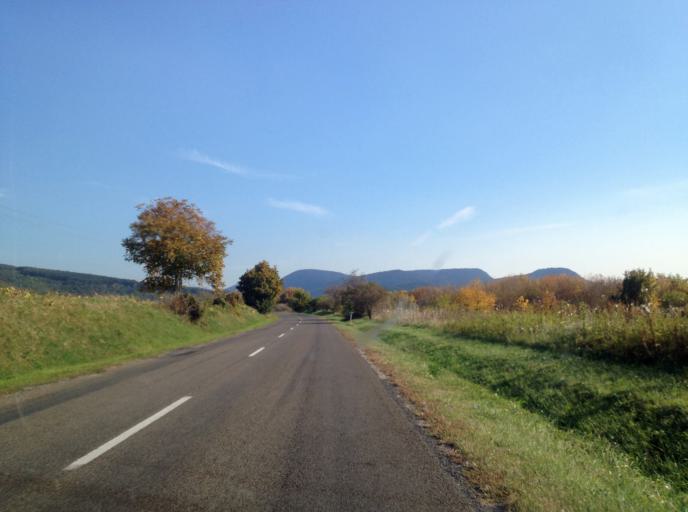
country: HU
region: Komarom-Esztergom
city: Esztergom
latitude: 47.7603
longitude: 18.7649
